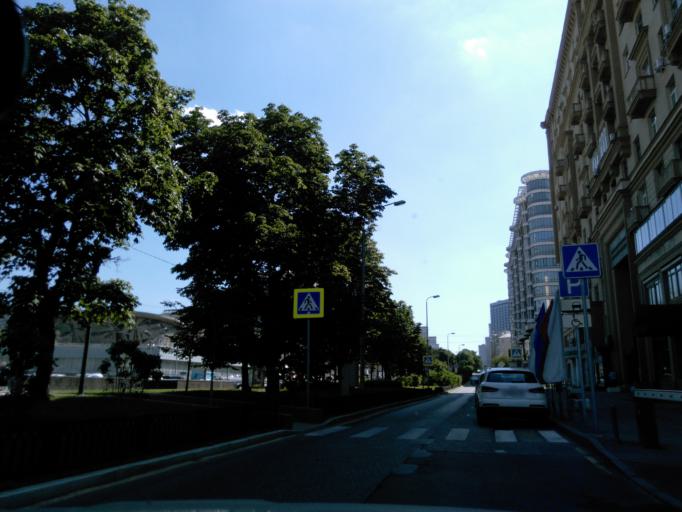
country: RU
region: Moskovskaya
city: Dorogomilovo
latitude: 55.7522
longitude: 37.5753
